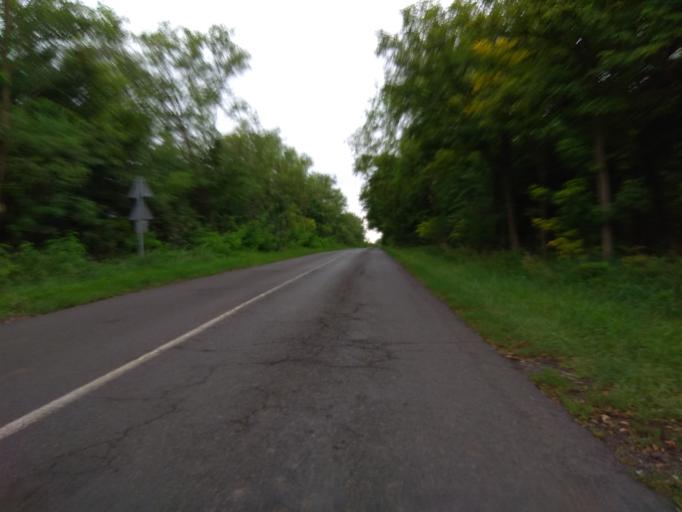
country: HU
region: Borsod-Abauj-Zemplen
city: Monok
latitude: 48.1743
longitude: 21.1122
